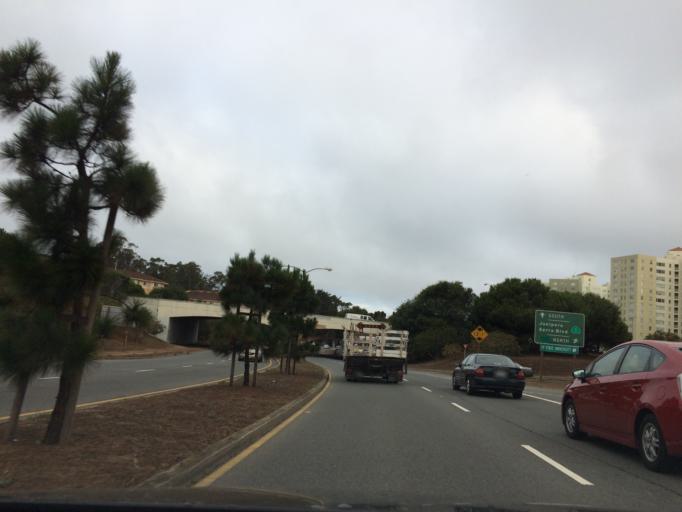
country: US
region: California
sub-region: San Mateo County
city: Daly City
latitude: 37.7127
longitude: -122.4698
